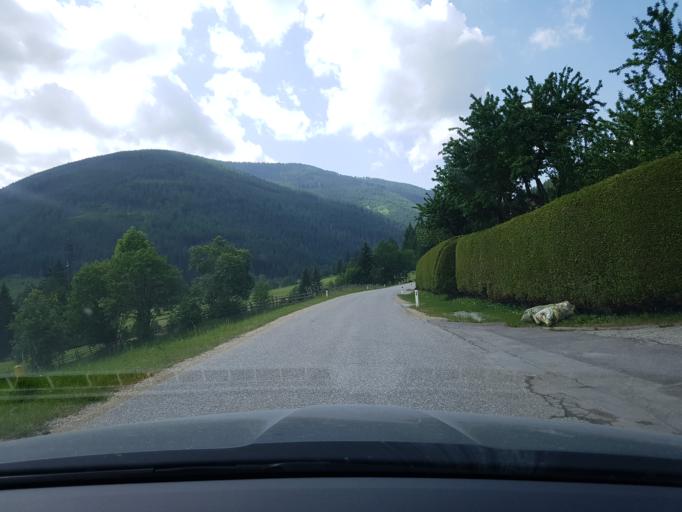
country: AT
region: Salzburg
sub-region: Politischer Bezirk Tamsweg
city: Thomatal
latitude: 47.0786
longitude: 13.7249
